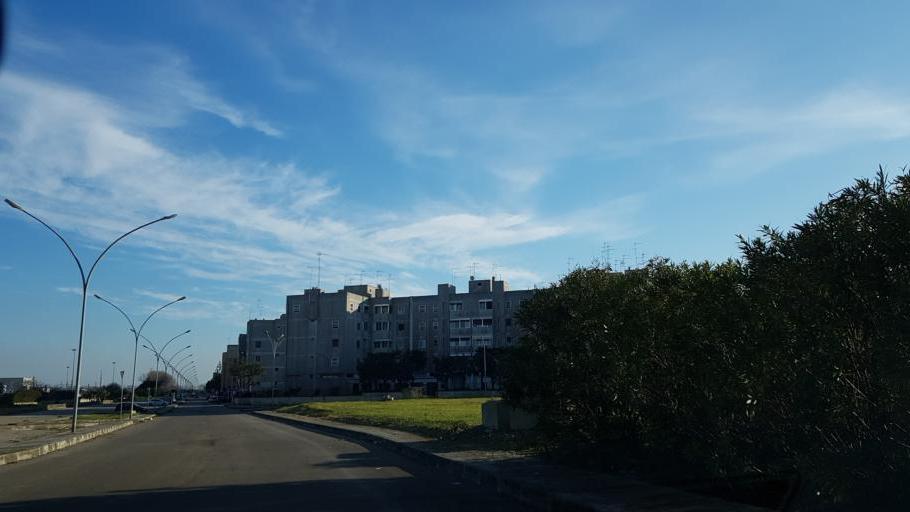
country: IT
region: Apulia
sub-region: Provincia di Brindisi
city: Brindisi
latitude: 40.6256
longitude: 17.9449
